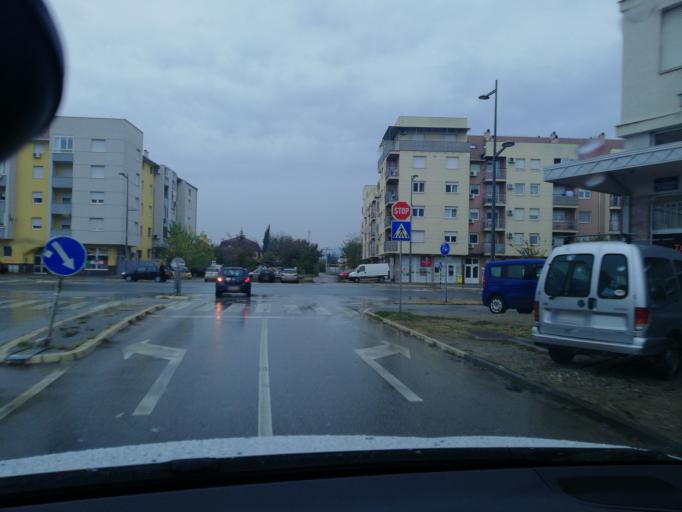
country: RS
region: Autonomna Pokrajina Vojvodina
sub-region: Juznobacki Okrug
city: Novi Sad
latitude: 45.2419
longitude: 19.8030
